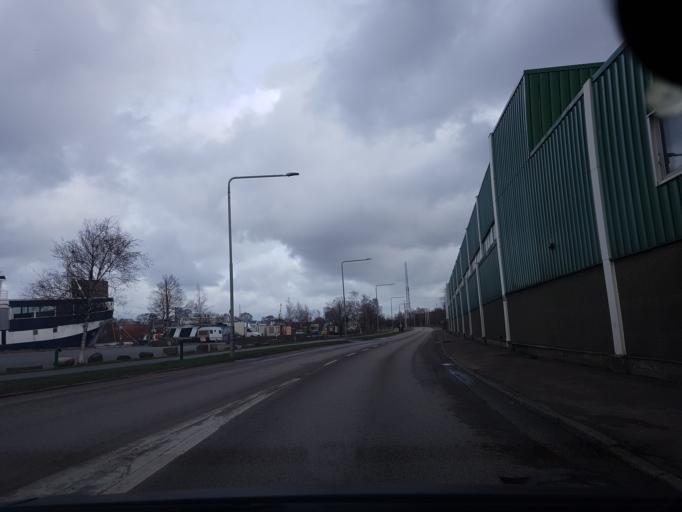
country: SE
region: Vaestra Goetaland
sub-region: Goteborg
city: Goeteborg
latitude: 57.7195
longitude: 11.9853
